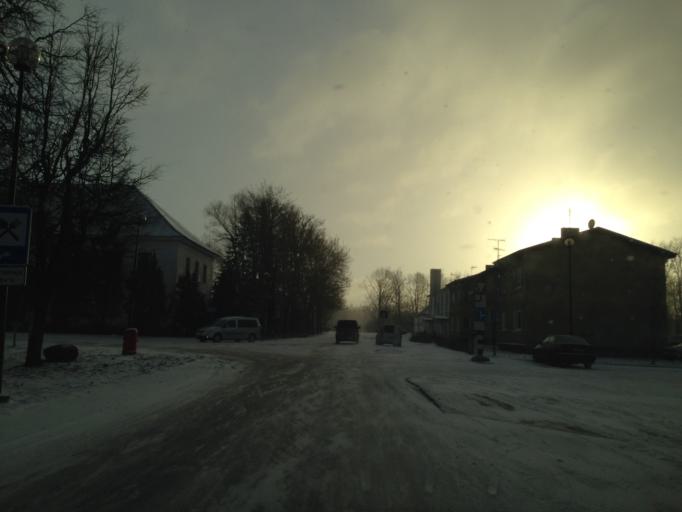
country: EE
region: Raplamaa
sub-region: Maerjamaa vald
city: Marjamaa
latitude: 58.9044
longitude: 24.4286
